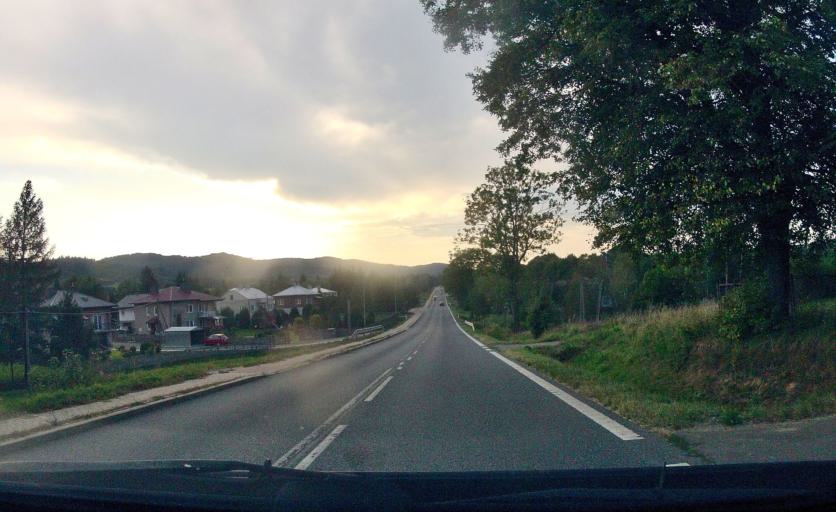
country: PL
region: Subcarpathian Voivodeship
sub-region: Powiat krosnienski
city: Dukla
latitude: 49.5616
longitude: 21.6087
